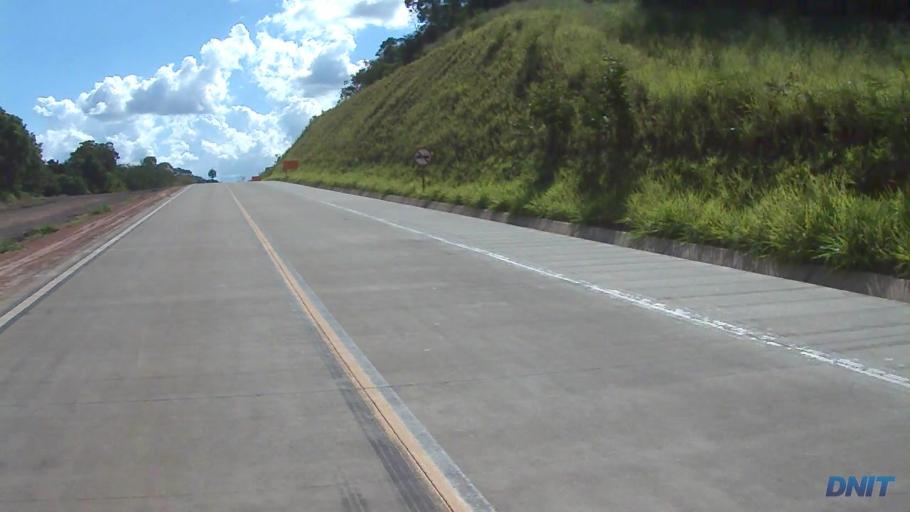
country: BR
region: Minas Gerais
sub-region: Barao De Cocais
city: Barao de Cocais
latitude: -19.7973
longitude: -43.4186
